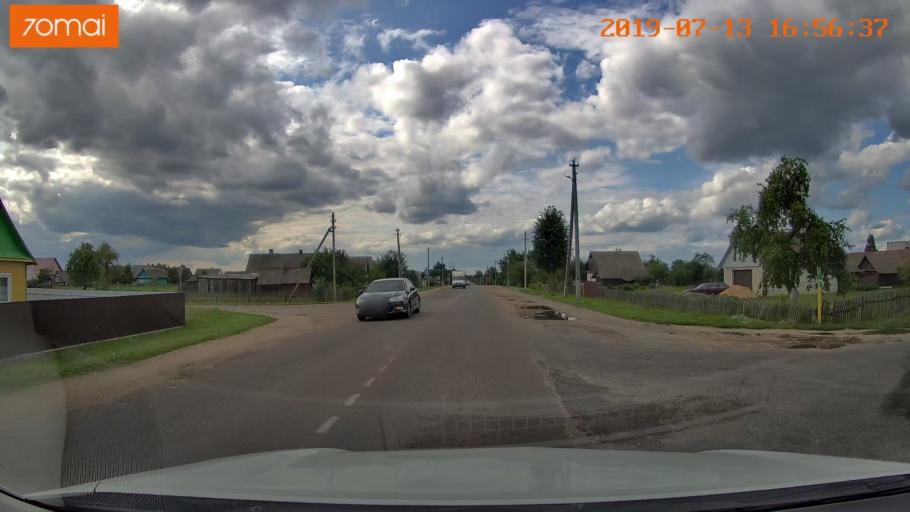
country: BY
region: Mogilev
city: Kirawsk
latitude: 53.2745
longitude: 29.4579
